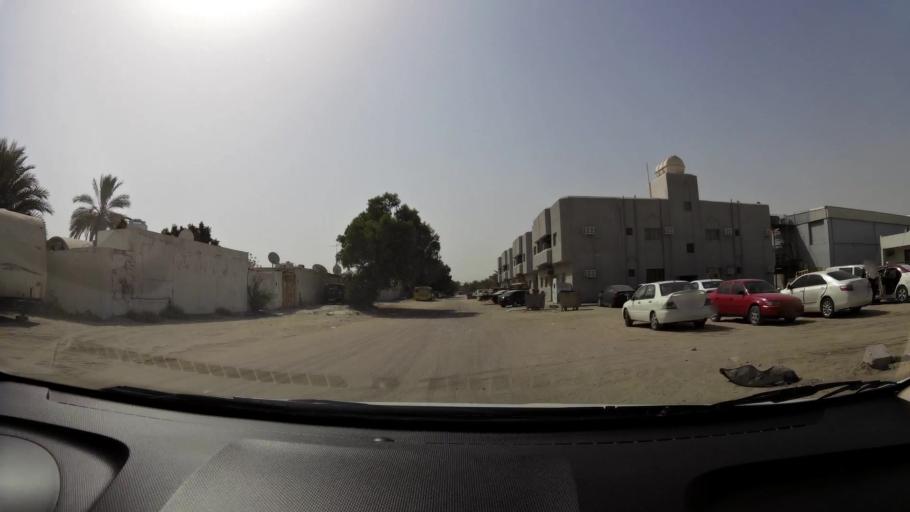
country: AE
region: Ash Shariqah
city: Sharjah
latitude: 25.3413
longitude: 55.4104
